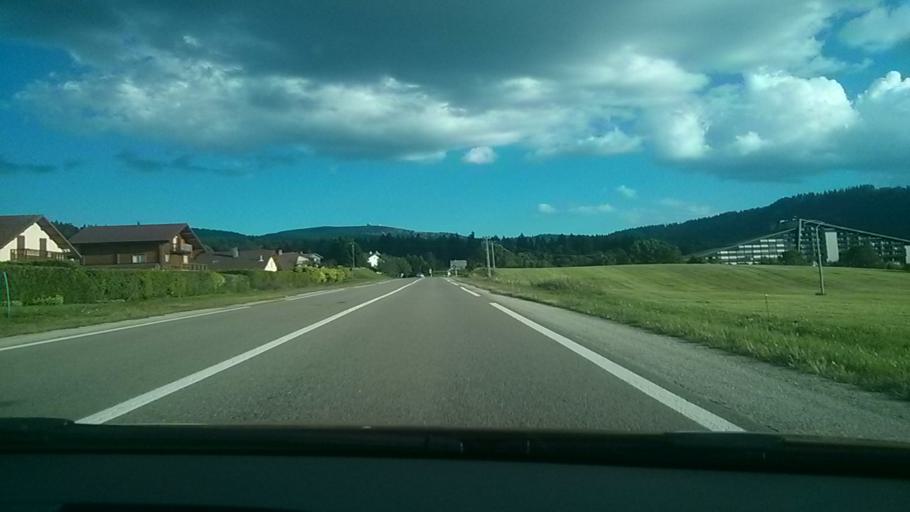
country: FR
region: Franche-Comte
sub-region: Departement du Jura
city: Les Rousses
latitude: 46.4655
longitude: 6.0706
